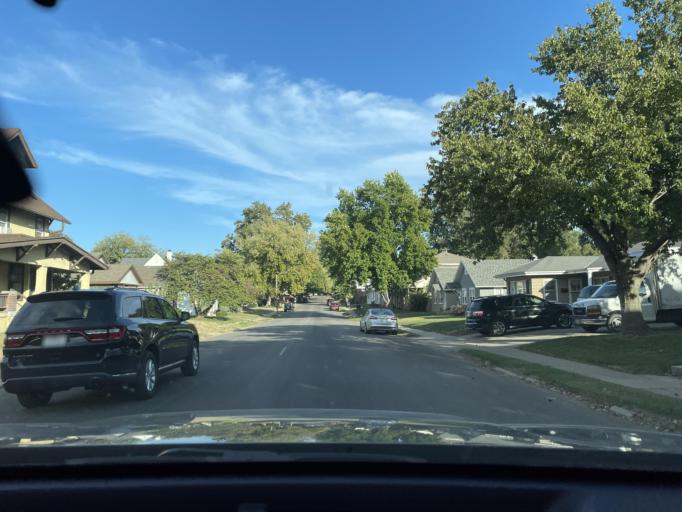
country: US
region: Missouri
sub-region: Buchanan County
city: Saint Joseph
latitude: 39.7683
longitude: -94.8245
